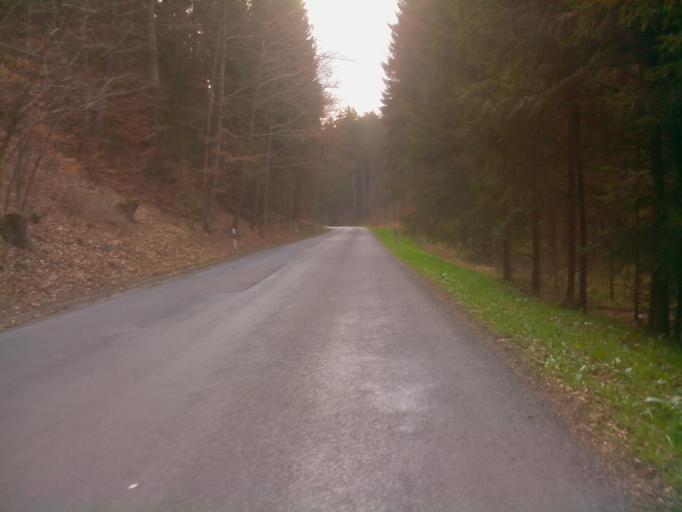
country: DE
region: Thuringia
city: Grosseutersdorf
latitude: 50.7665
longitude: 11.5739
